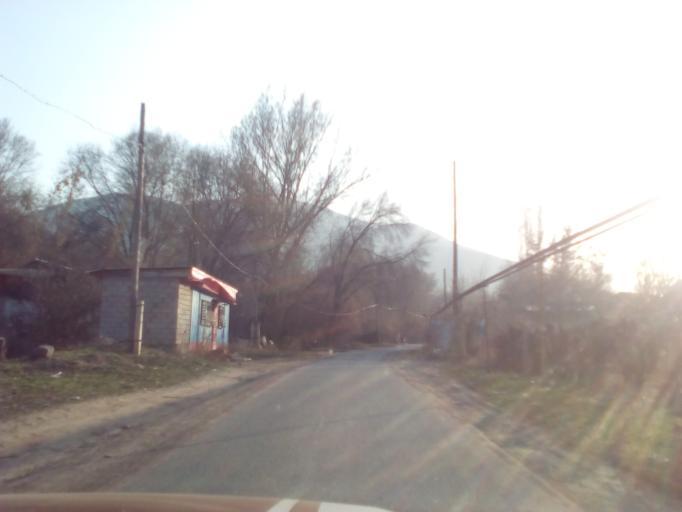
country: KZ
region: Almaty Oblysy
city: Burunday
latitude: 43.1561
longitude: 76.4333
